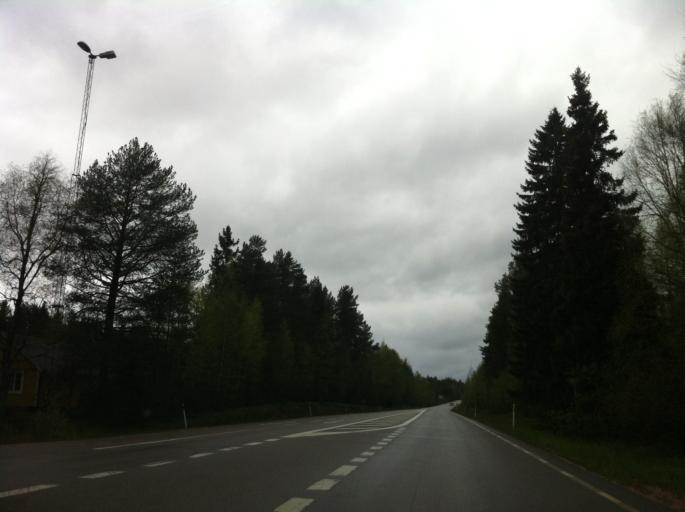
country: SE
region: Jaemtland
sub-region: Harjedalens Kommun
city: Sveg
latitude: 62.0461
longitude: 14.3431
